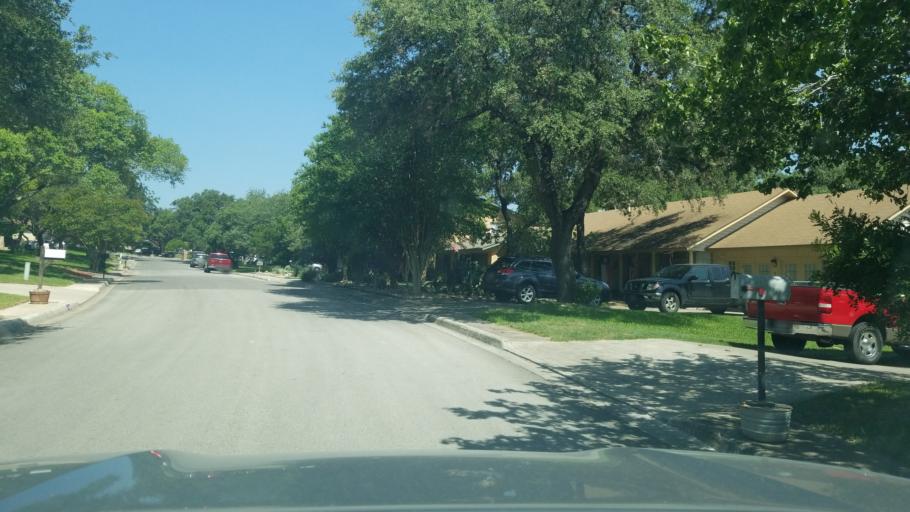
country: US
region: Texas
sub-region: Bexar County
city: Hollywood Park
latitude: 29.5884
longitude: -98.4601
